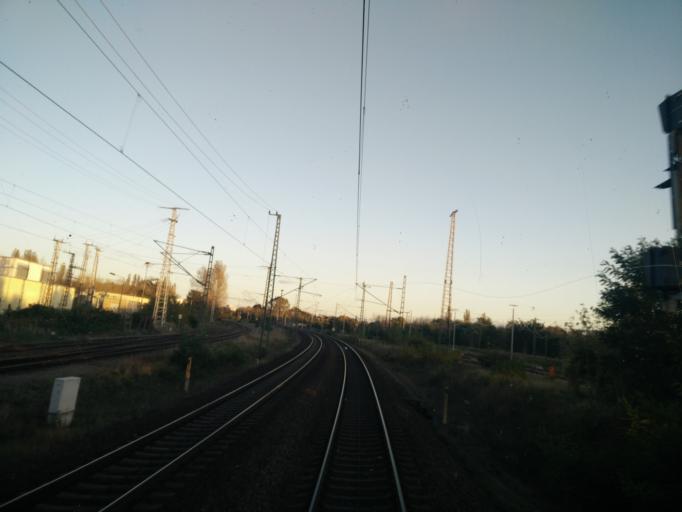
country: DE
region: Brandenburg
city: Wittenberge
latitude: 52.9967
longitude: 11.7671
